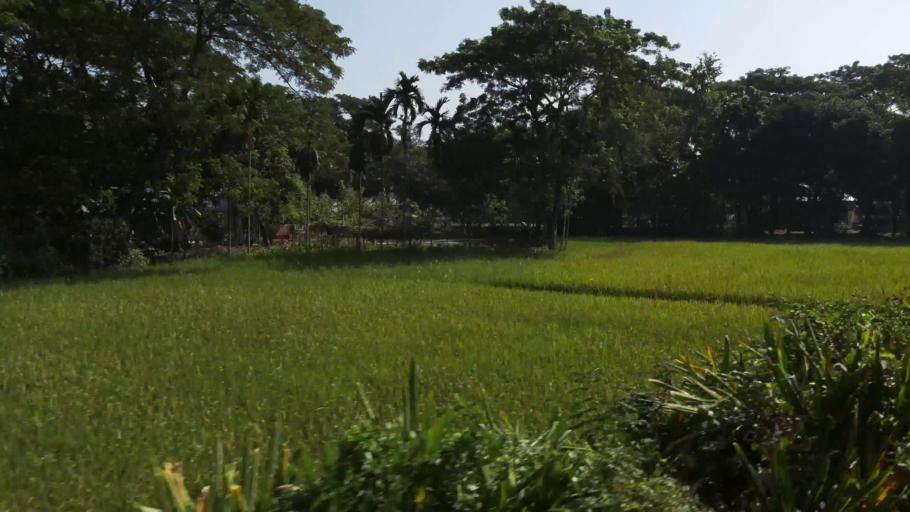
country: BD
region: Dhaka
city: Gafargaon
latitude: 24.5393
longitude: 90.5086
